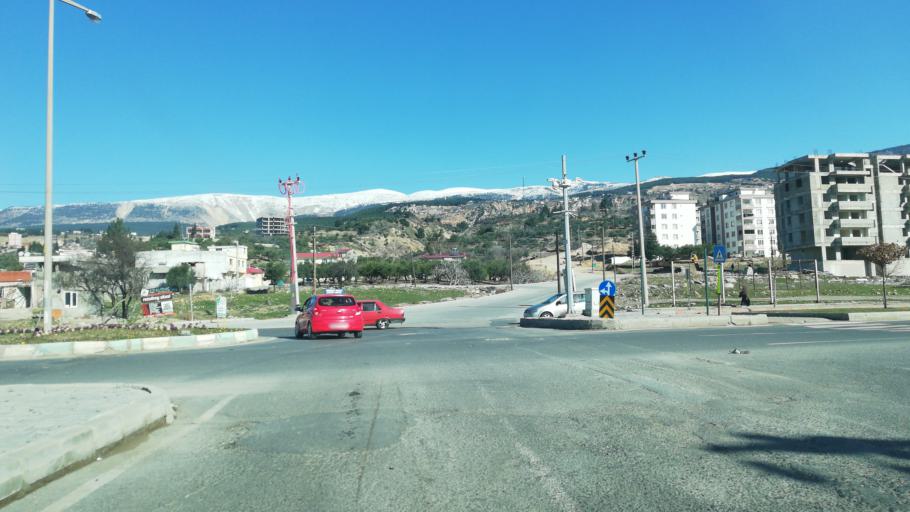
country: TR
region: Kahramanmaras
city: Kahramanmaras
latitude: 37.5820
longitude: 36.9745
